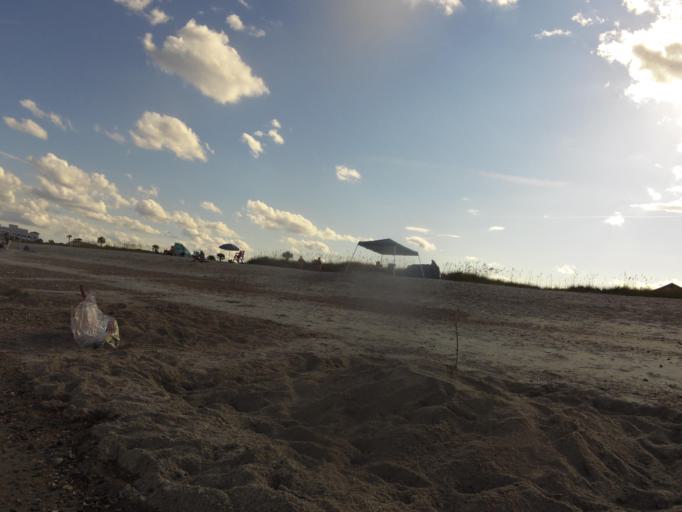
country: US
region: Florida
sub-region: Nassau County
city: Fernandina Beach
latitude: 30.6707
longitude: -81.4296
